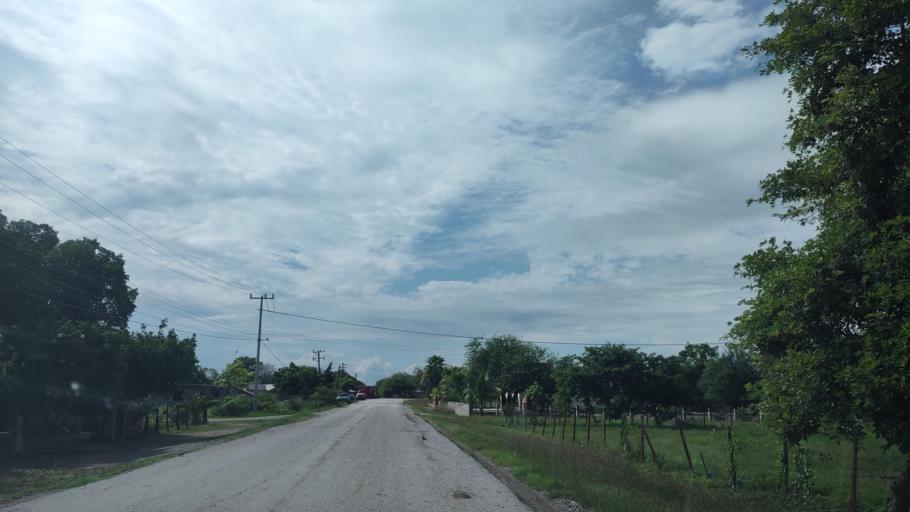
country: MX
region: Veracruz
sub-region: Panuco
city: Oviedo
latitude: 22.0033
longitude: -98.4598
